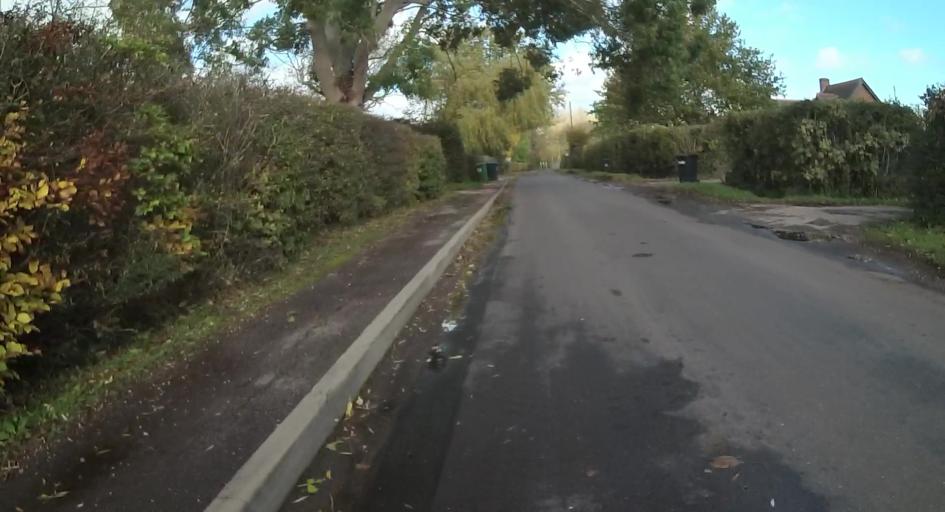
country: GB
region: England
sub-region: West Berkshire
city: Stratfield Mortimer
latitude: 51.3520
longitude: -1.0175
